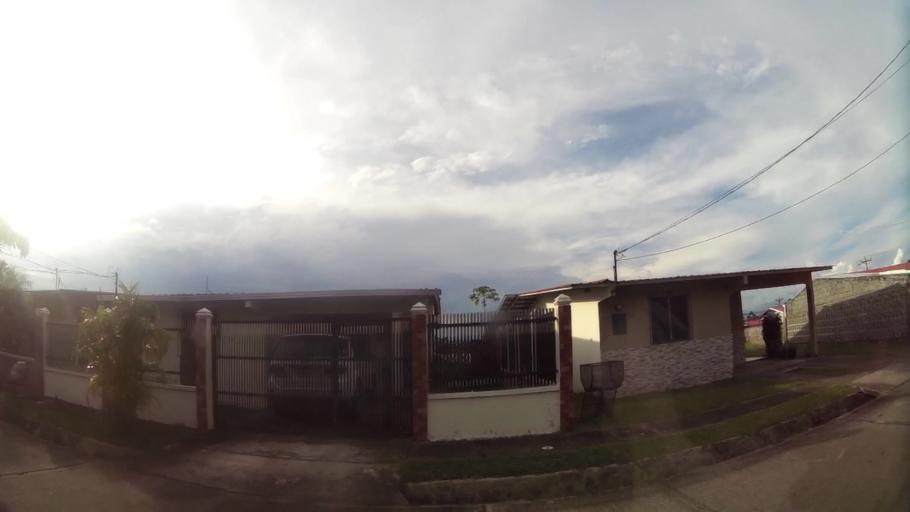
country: PA
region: Panama
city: La Chorrera
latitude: 8.8959
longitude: -79.7678
